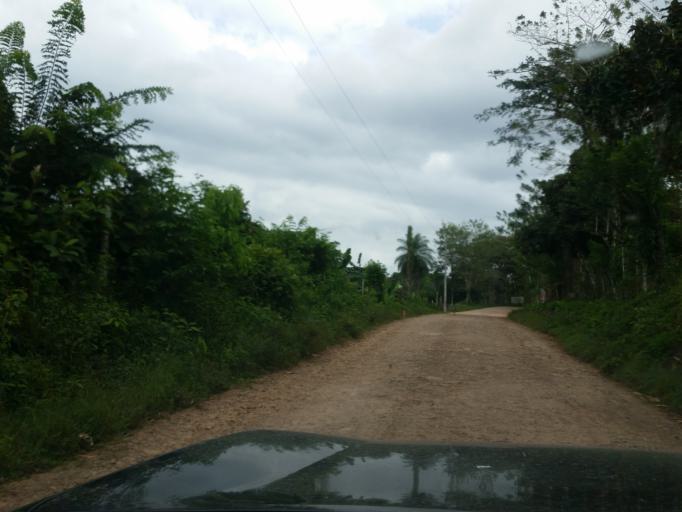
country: CR
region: Alajuela
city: Los Chiles
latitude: 11.1190
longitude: -84.5999
